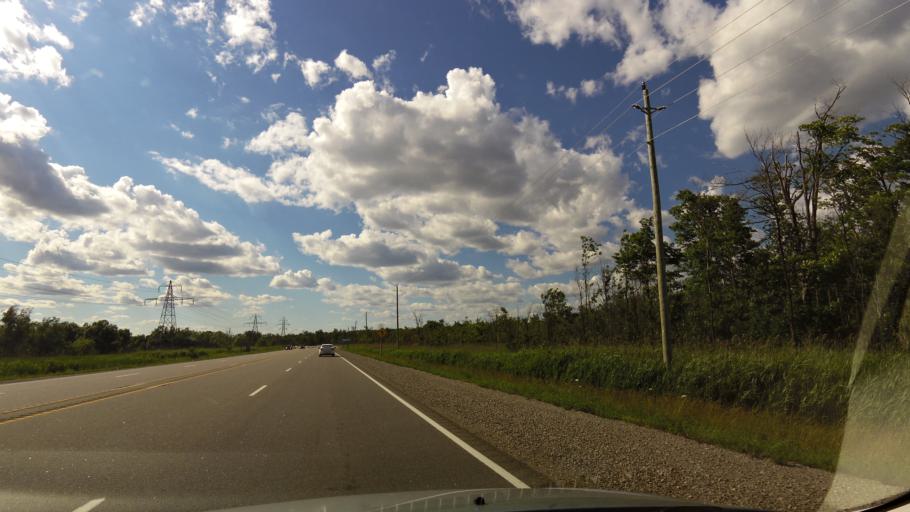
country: CA
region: Ontario
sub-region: Halton
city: Milton
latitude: 43.4065
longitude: -80.0449
